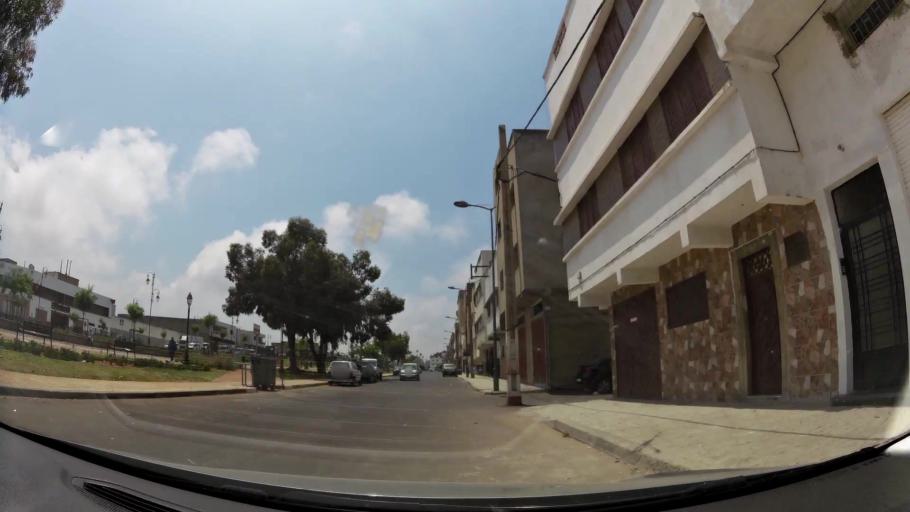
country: MA
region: Rabat-Sale-Zemmour-Zaer
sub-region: Rabat
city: Rabat
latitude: 33.9852
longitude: -6.8751
